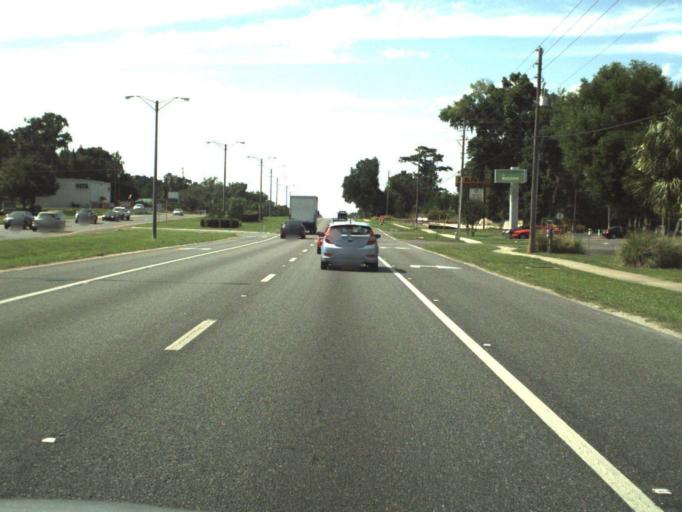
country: US
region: Florida
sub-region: Marion County
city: Belleview
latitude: 29.0658
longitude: -82.0682
